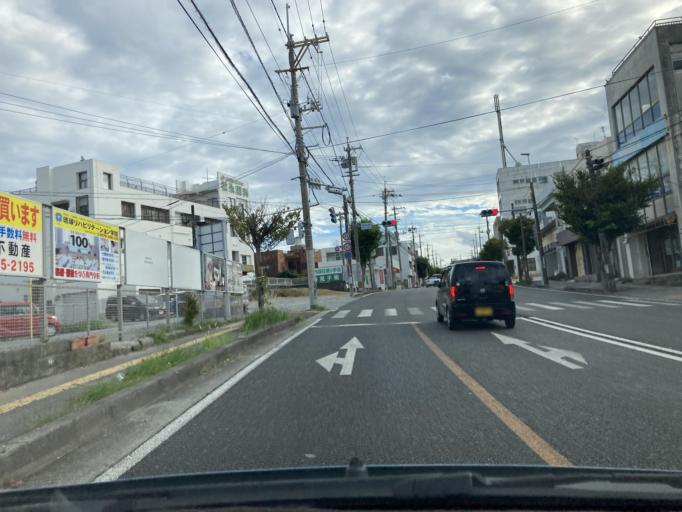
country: JP
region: Okinawa
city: Okinawa
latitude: 26.3452
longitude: 127.8135
